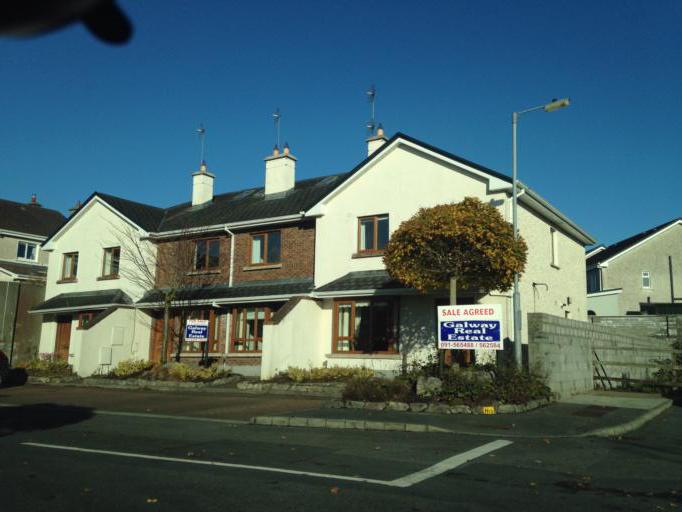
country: IE
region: Connaught
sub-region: County Galway
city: Oranmore
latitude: 53.2750
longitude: -8.9724
